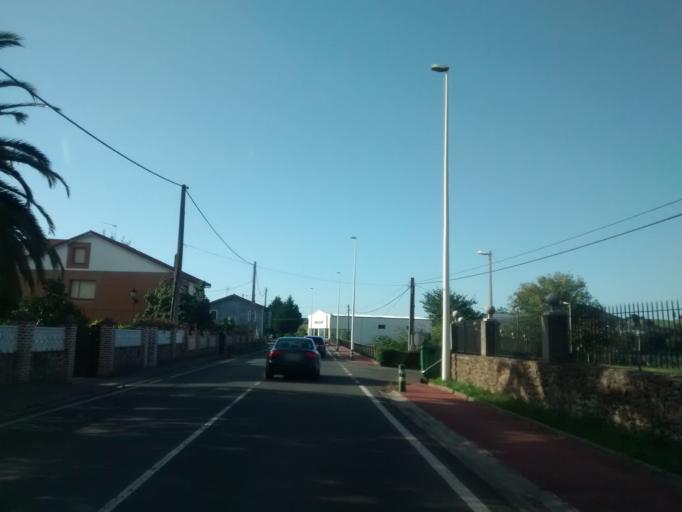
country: ES
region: Cantabria
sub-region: Provincia de Cantabria
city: Lierganes
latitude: 43.3951
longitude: -3.7308
